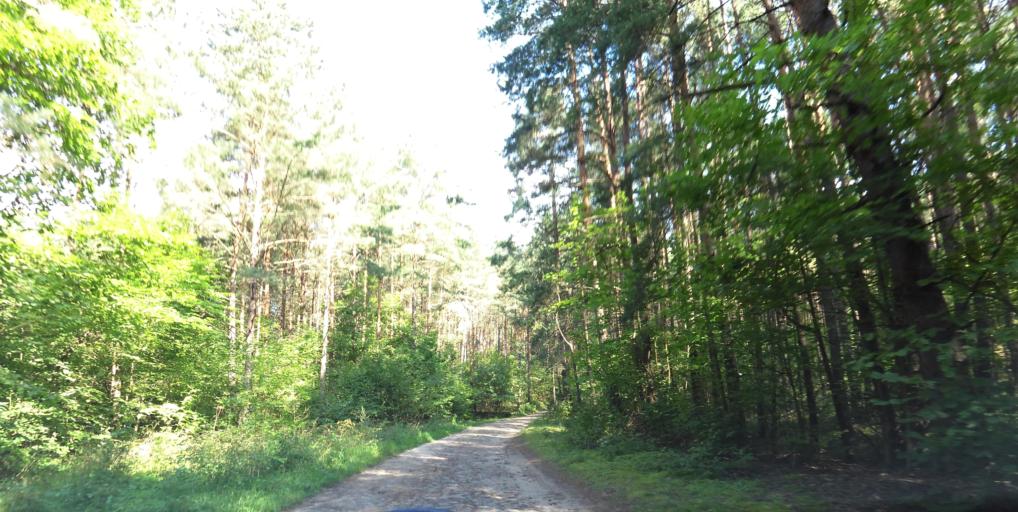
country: LT
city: Grigiskes
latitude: 54.7357
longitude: 25.0401
